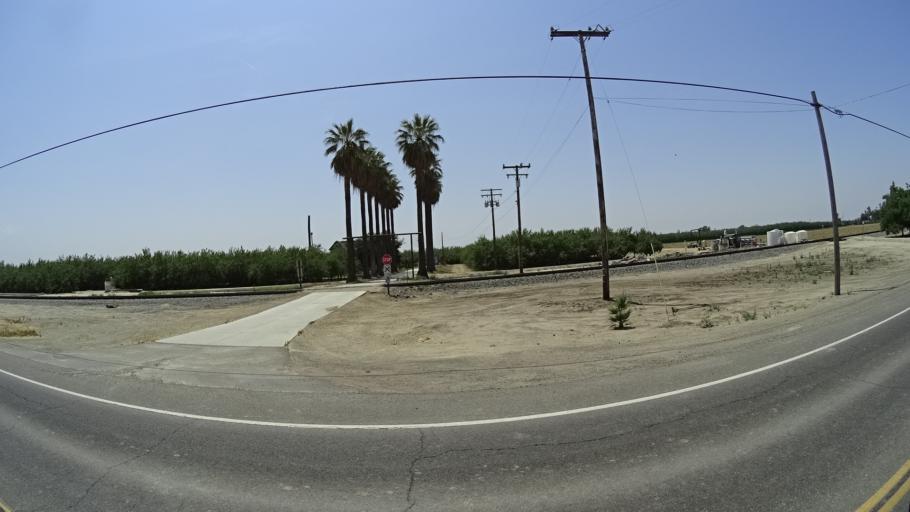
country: US
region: California
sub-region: Kings County
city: Armona
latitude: 36.3135
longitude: -119.7219
